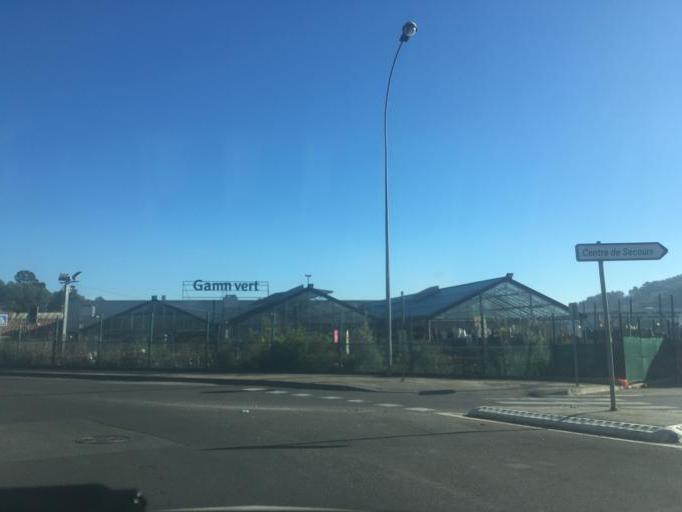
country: FR
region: Provence-Alpes-Cote d'Azur
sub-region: Departement du Var
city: Draguignan
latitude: 43.5264
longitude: 6.4553
